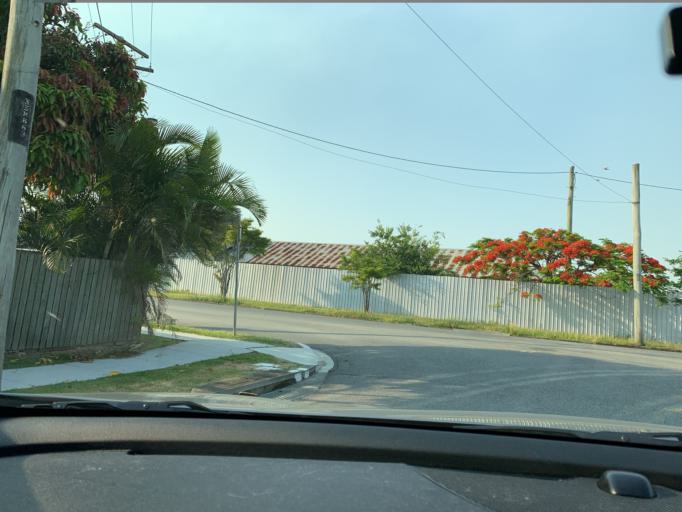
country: AU
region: Queensland
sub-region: Brisbane
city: Ascot
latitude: -27.4295
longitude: 153.0784
